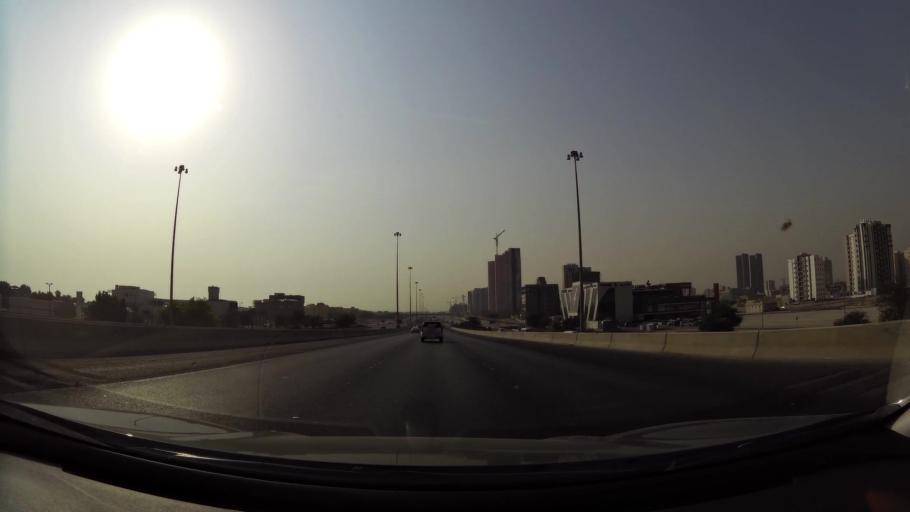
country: KW
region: Mubarak al Kabir
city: Sabah as Salim
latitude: 29.2663
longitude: 48.0855
